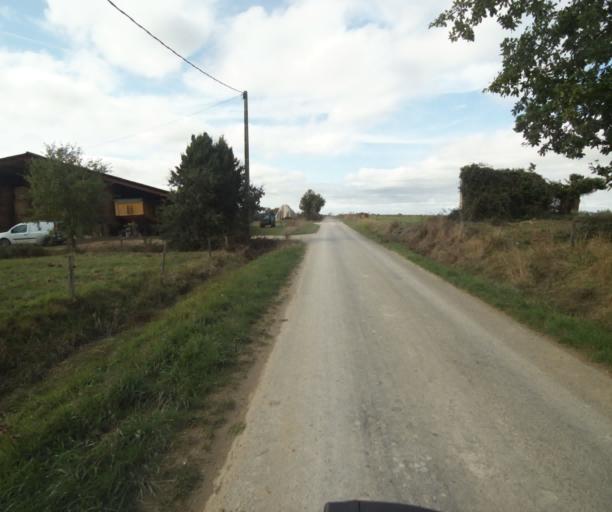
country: FR
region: Midi-Pyrenees
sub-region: Departement du Tarn-et-Garonne
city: Saint-Porquier
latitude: 43.9601
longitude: 1.1484
